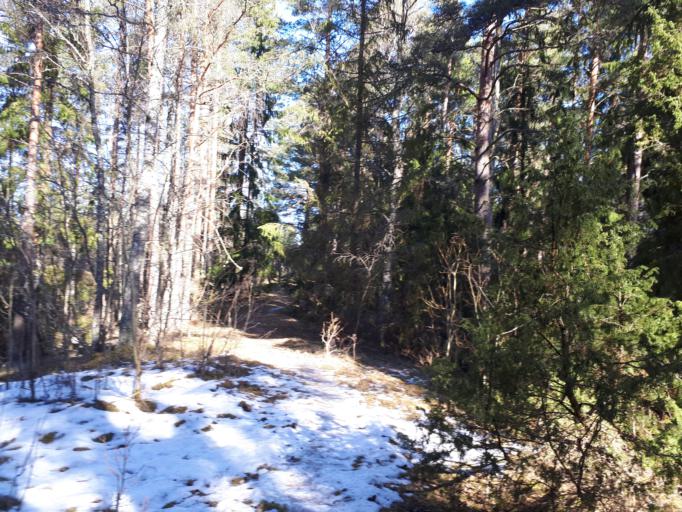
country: SE
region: Soedermanland
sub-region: Flens Kommun
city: Halleforsnas
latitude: 59.0832
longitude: 16.3659
